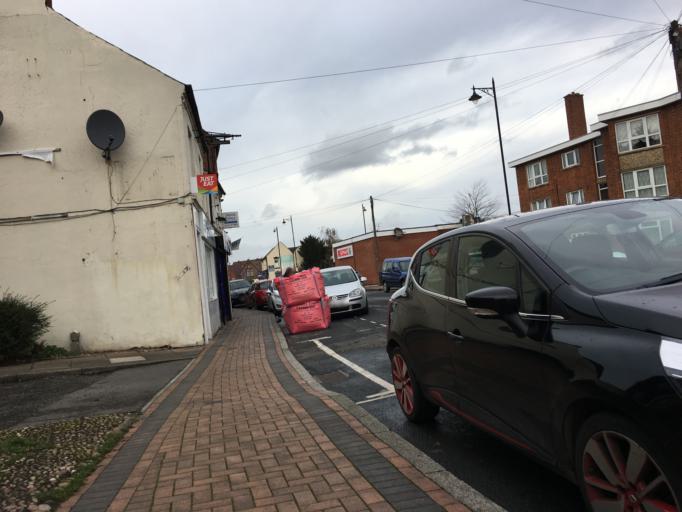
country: GB
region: England
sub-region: Warwickshire
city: Nuneaton
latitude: 52.5267
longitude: -1.4744
